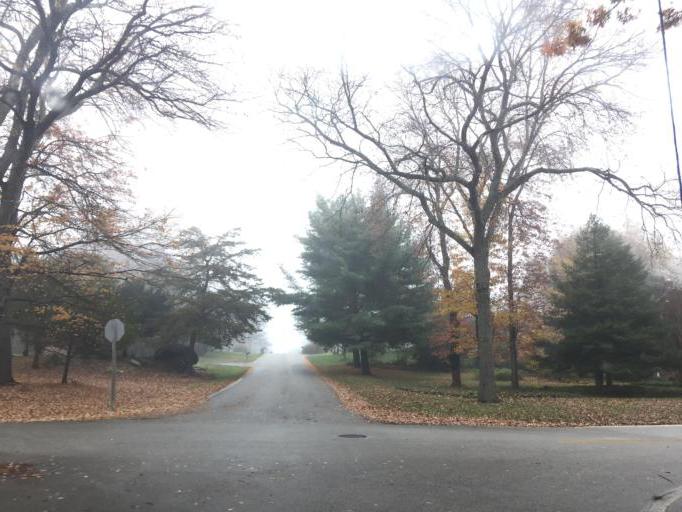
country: US
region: Maryland
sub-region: Howard County
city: Riverside
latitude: 39.1876
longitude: -76.8584
